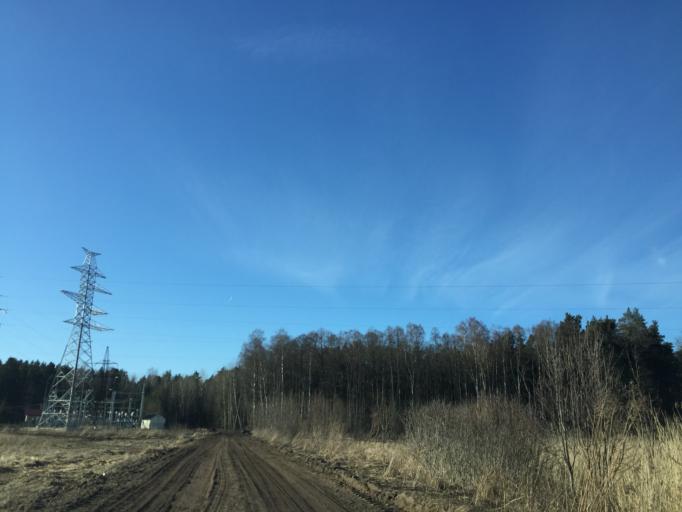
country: LV
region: Babite
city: Pinki
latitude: 56.9658
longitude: 23.8866
